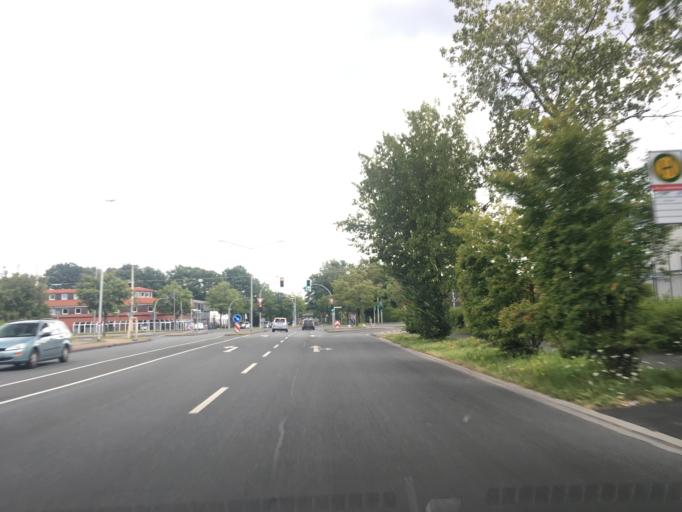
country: DE
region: North Rhine-Westphalia
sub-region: Regierungsbezirk Munster
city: Muenster
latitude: 51.9294
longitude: 7.6472
